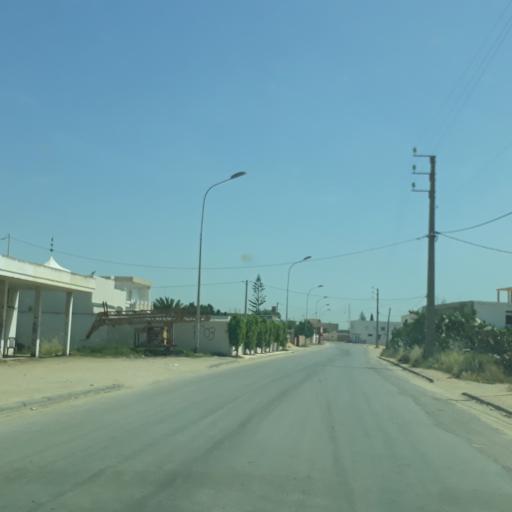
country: TN
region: Safaqis
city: Al Qarmadah
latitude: 34.8123
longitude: 10.7678
